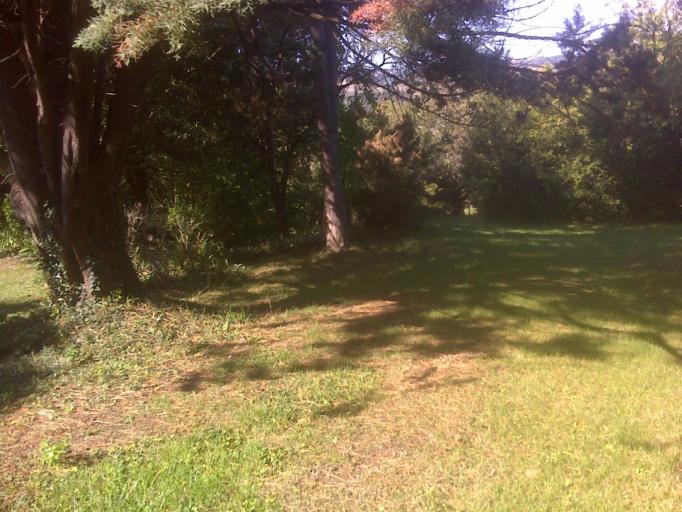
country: FR
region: Midi-Pyrenees
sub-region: Departement du Gers
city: Lectoure
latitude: 43.9310
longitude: 0.6252
